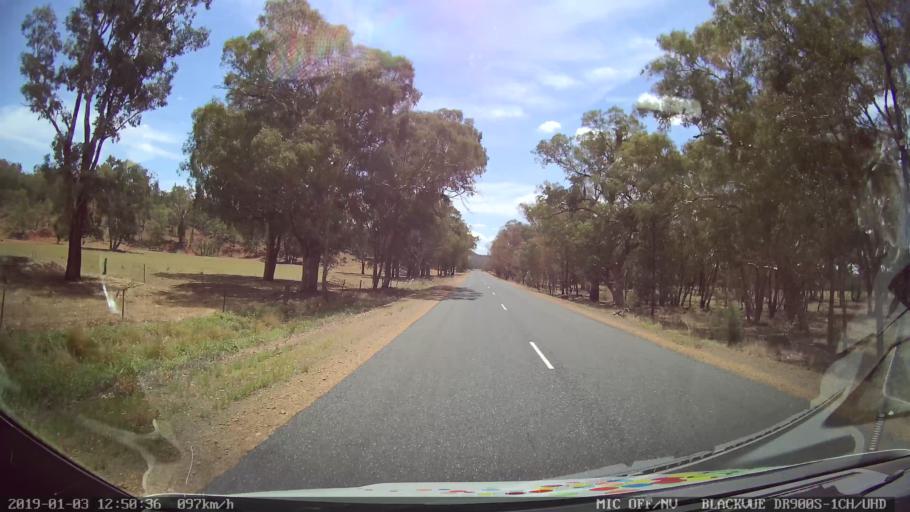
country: AU
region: New South Wales
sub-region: Weddin
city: Grenfell
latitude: -33.6898
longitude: 148.2722
